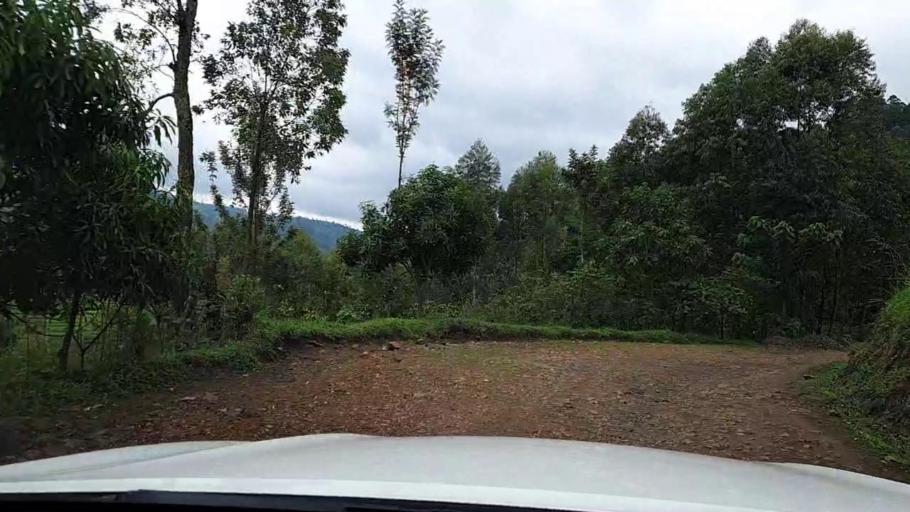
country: RW
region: Western Province
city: Cyangugu
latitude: -2.5585
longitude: 29.0352
